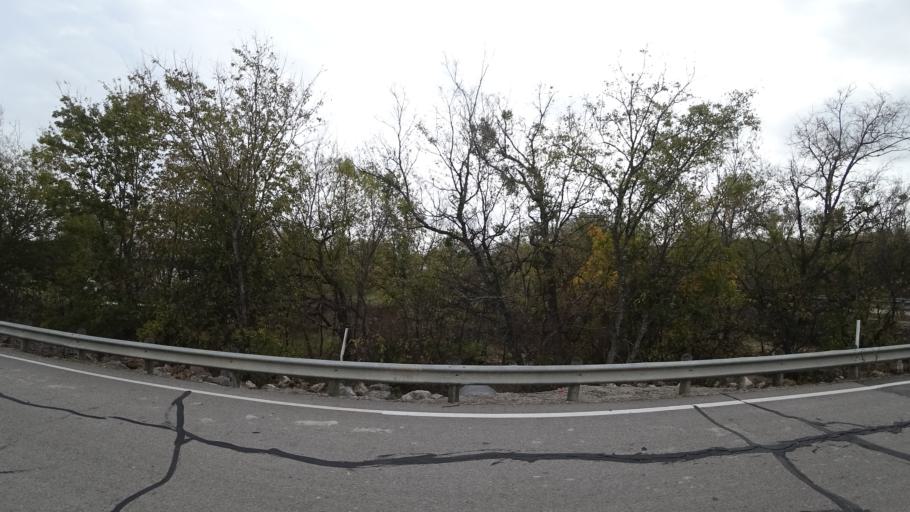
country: US
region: Texas
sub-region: Travis County
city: Manor
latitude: 30.3744
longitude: -97.5619
